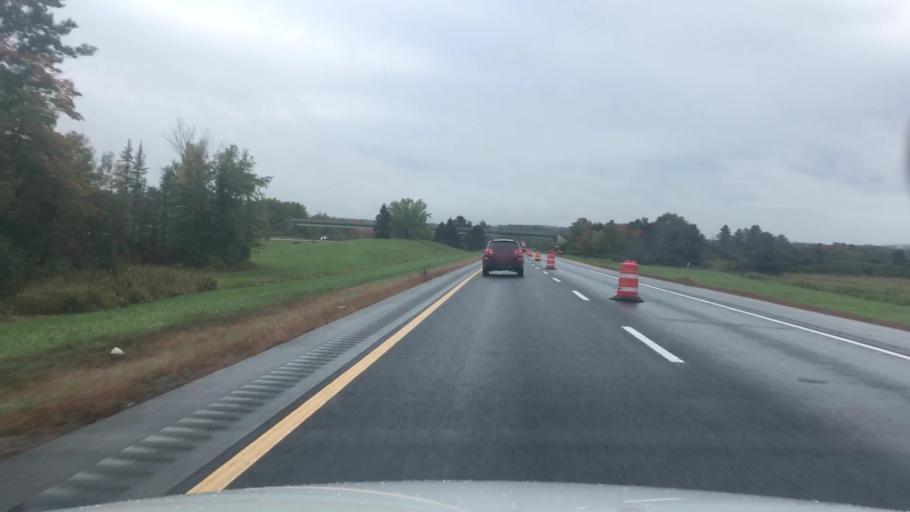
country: US
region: Maine
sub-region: Sagadahoc County
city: Richmond
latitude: 44.1473
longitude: -69.8398
